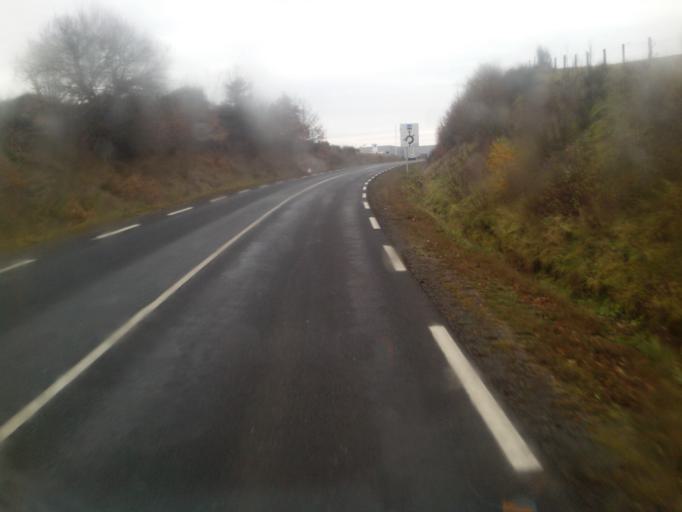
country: FR
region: Auvergne
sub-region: Departement du Cantal
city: Saint-Flour
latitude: 45.0335
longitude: 3.1262
